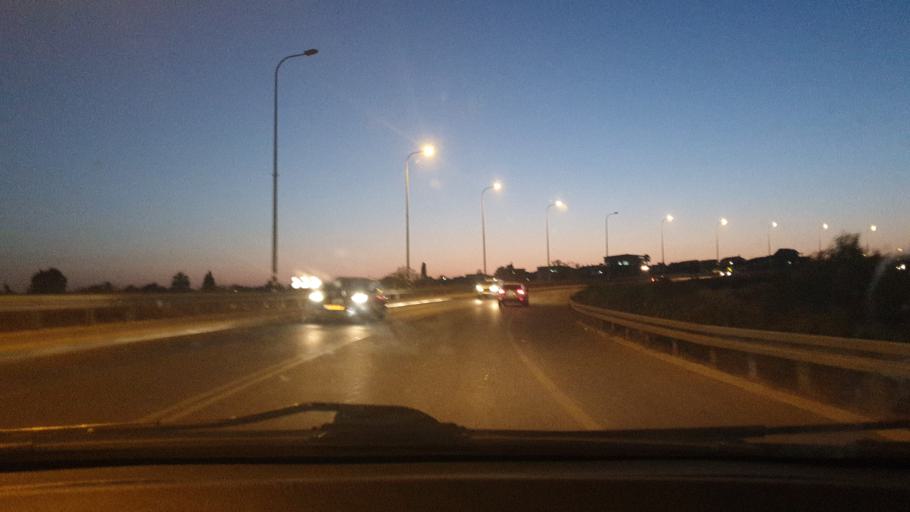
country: IL
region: Central District
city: Bene 'Ayish
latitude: 31.7925
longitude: 34.7666
